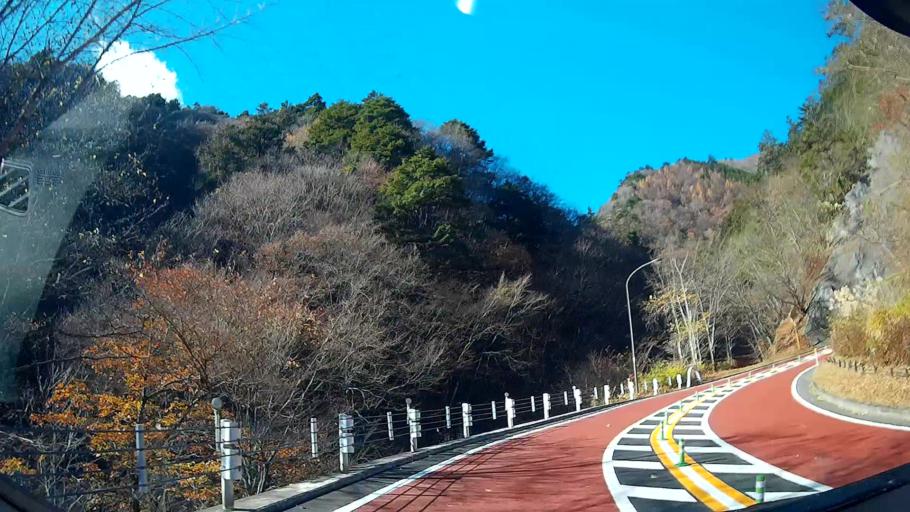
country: JP
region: Yamanashi
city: Uenohara
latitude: 35.7351
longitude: 139.0307
